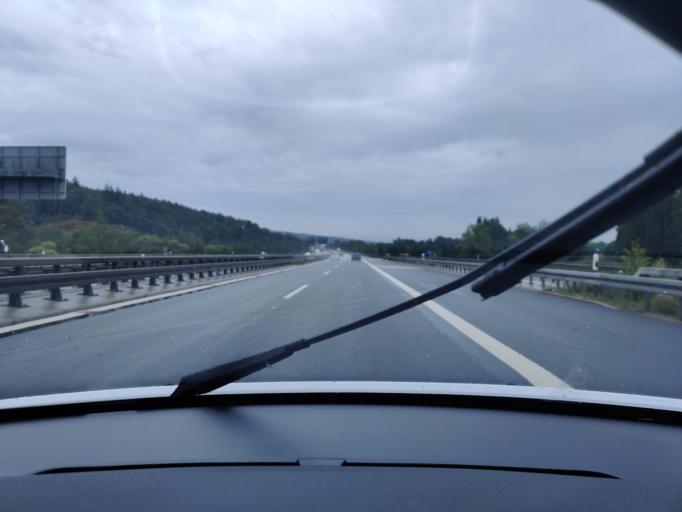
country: DE
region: Bavaria
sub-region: Upper Palatinate
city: Wernberg-Koblitz
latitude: 49.5160
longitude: 12.1666
